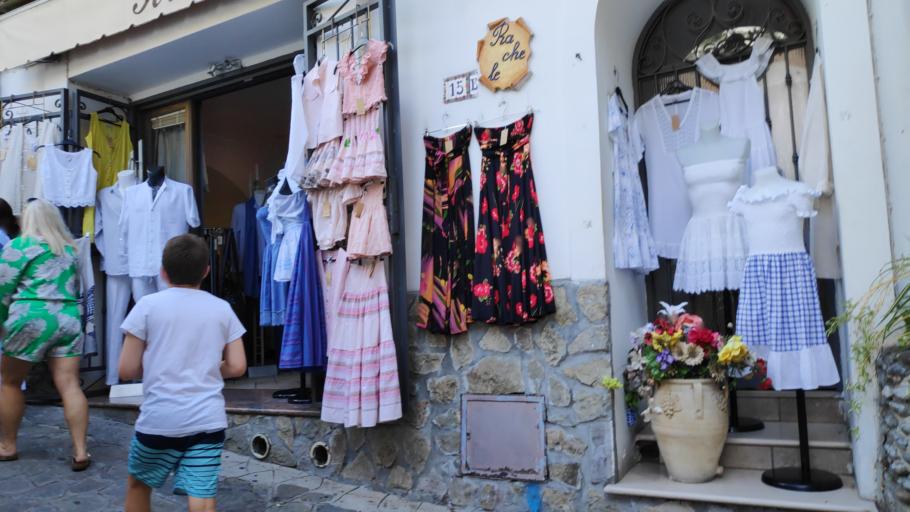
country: IT
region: Campania
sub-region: Provincia di Salerno
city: Positano
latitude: 40.6293
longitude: 14.4866
